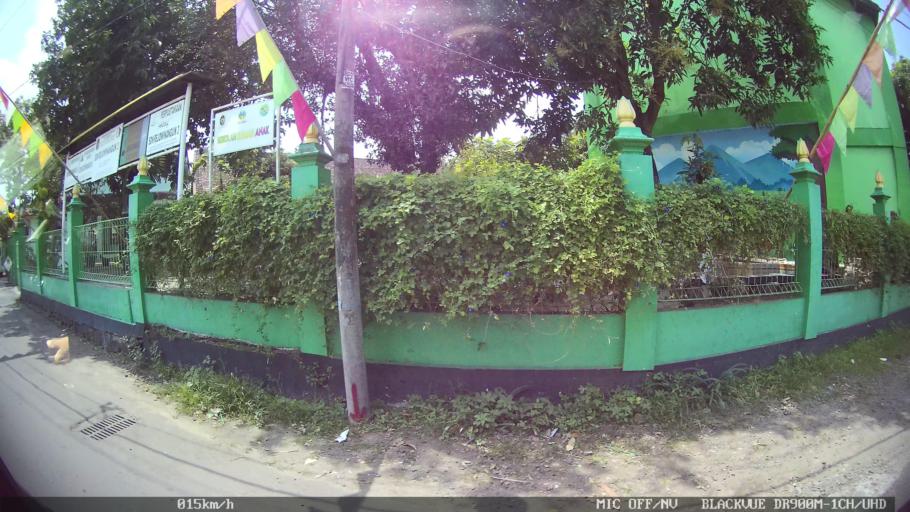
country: ID
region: Daerah Istimewa Yogyakarta
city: Yogyakarta
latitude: -7.8180
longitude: 110.3948
